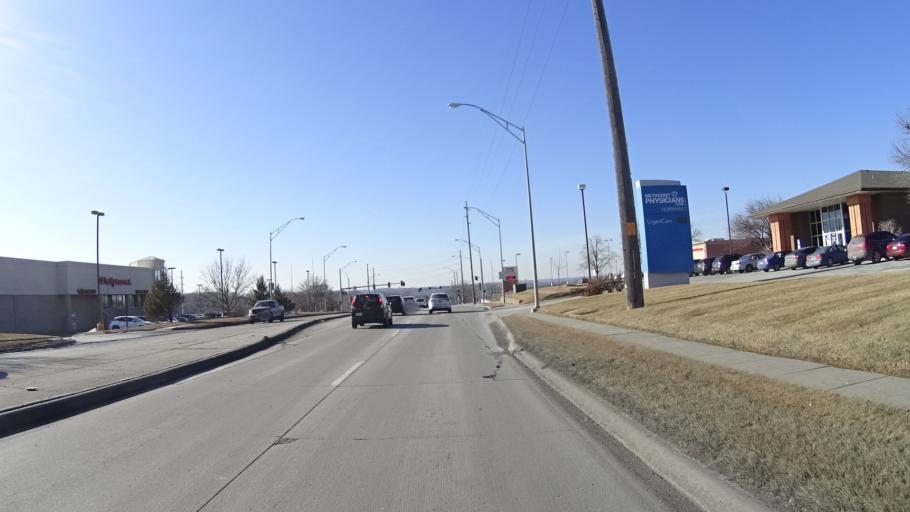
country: US
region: Nebraska
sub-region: Douglas County
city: Bennington
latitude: 41.3067
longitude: -96.0793
